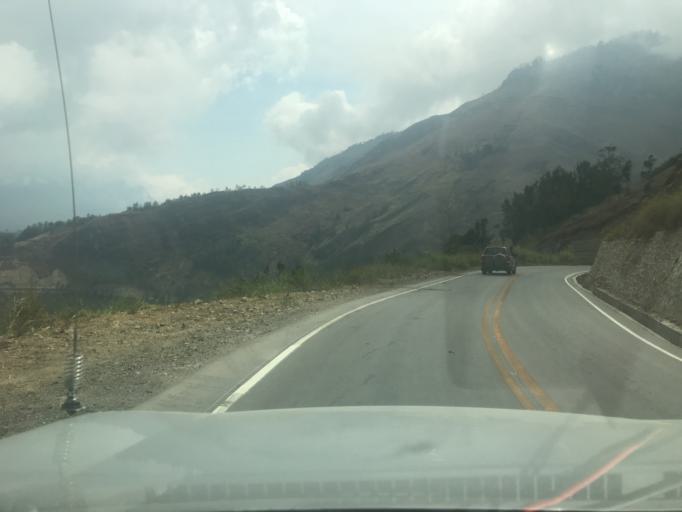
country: TL
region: Manufahi
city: Same
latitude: -8.8916
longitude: 125.5937
